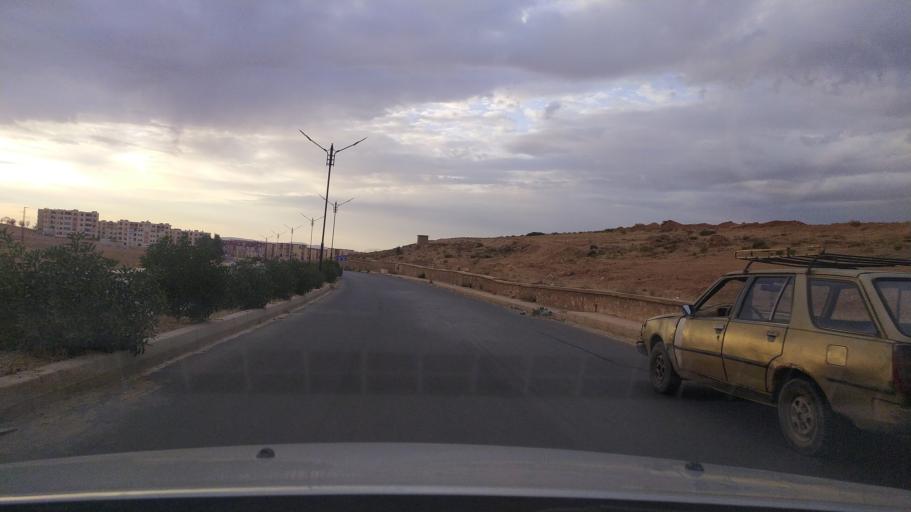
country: DZ
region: Tiaret
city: Frenda
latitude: 35.0522
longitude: 1.0669
